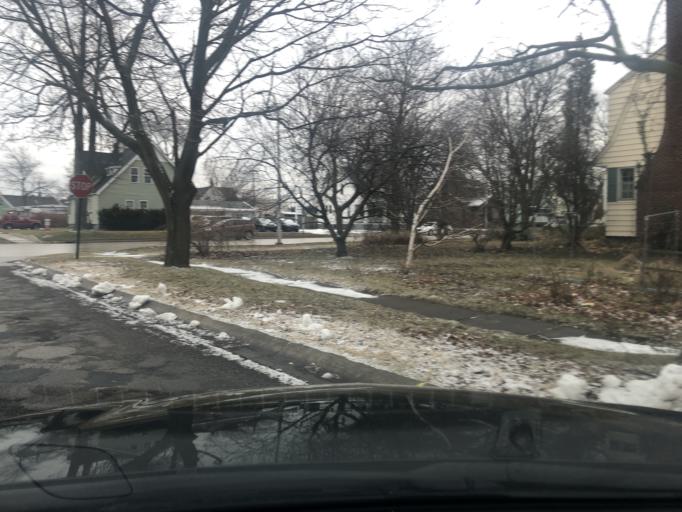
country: US
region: Michigan
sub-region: Saint Clair County
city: Port Huron
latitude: 42.9932
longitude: -82.4347
